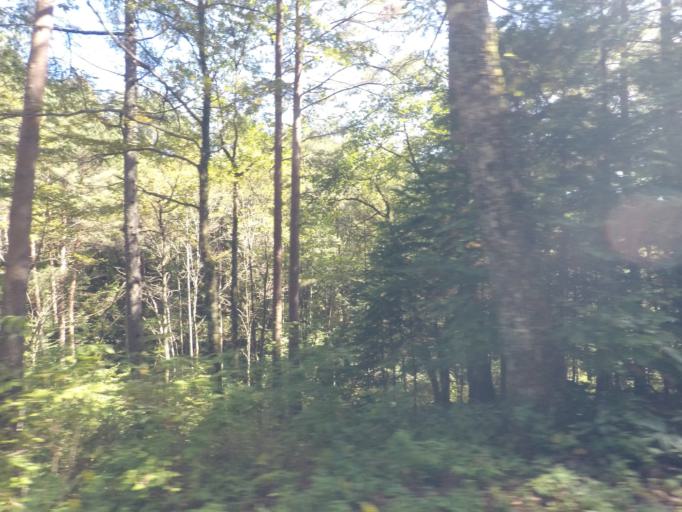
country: JP
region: Nagano
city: Shiojiri
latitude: 35.9957
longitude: 137.7356
